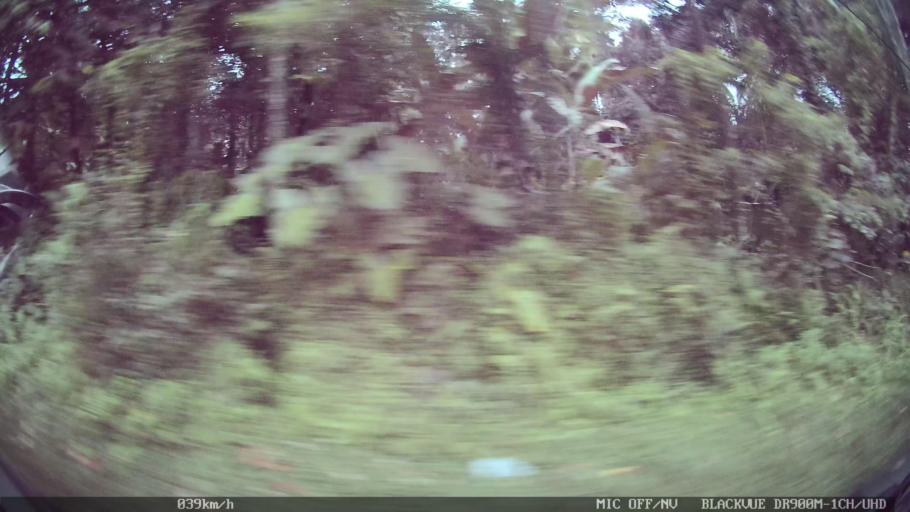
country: ID
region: Bali
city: Pegongan
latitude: -8.4790
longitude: 115.2301
